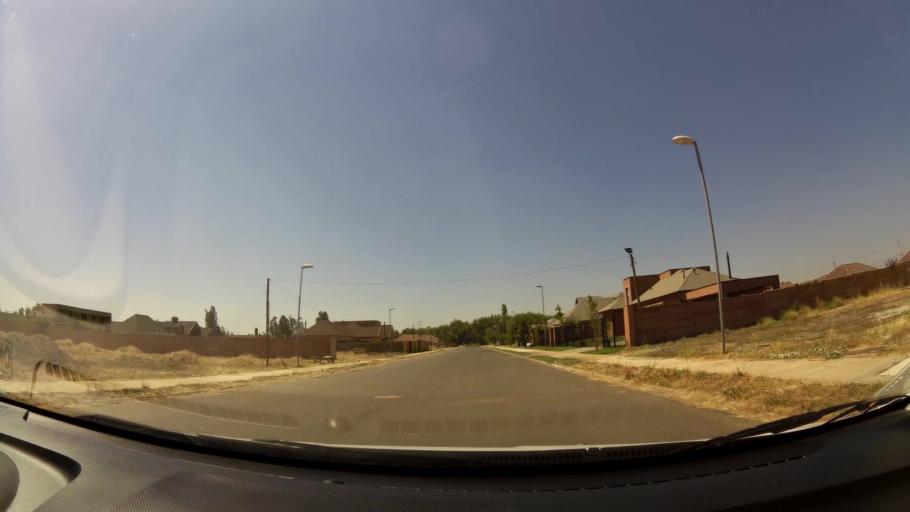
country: CL
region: Maule
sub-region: Provincia de Talca
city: Talca
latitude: -35.4308
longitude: -71.5993
